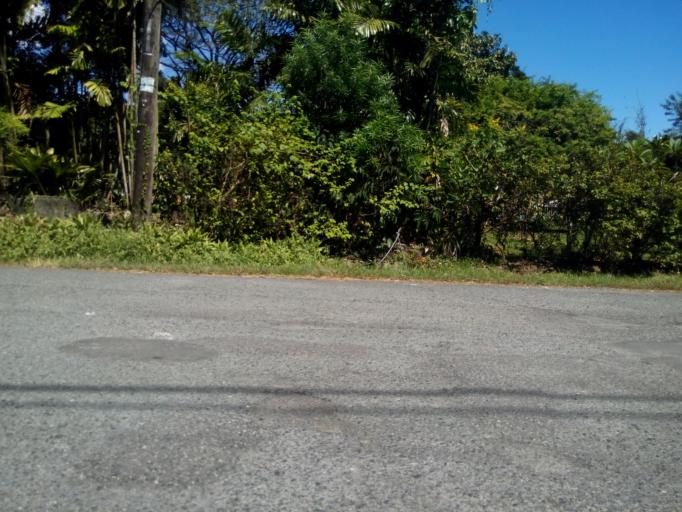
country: PH
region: Metro Manila
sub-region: Quezon City
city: Quezon City
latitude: 14.6455
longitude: 121.0687
